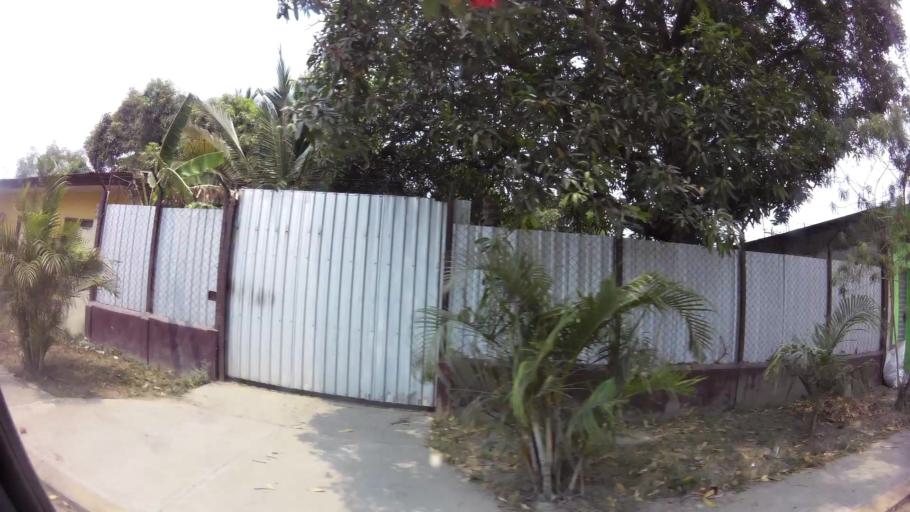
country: HN
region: Yoro
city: El Progreso
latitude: 15.4000
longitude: -87.8039
